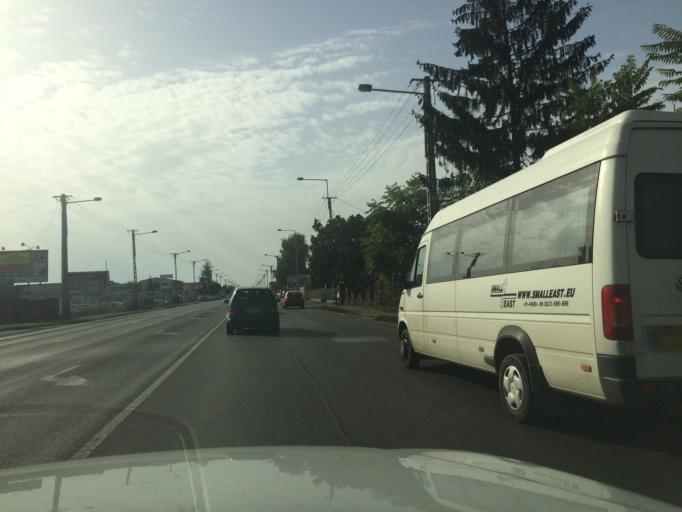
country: HU
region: Szabolcs-Szatmar-Bereg
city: Nyiregyhaza
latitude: 47.9330
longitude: 21.7187
